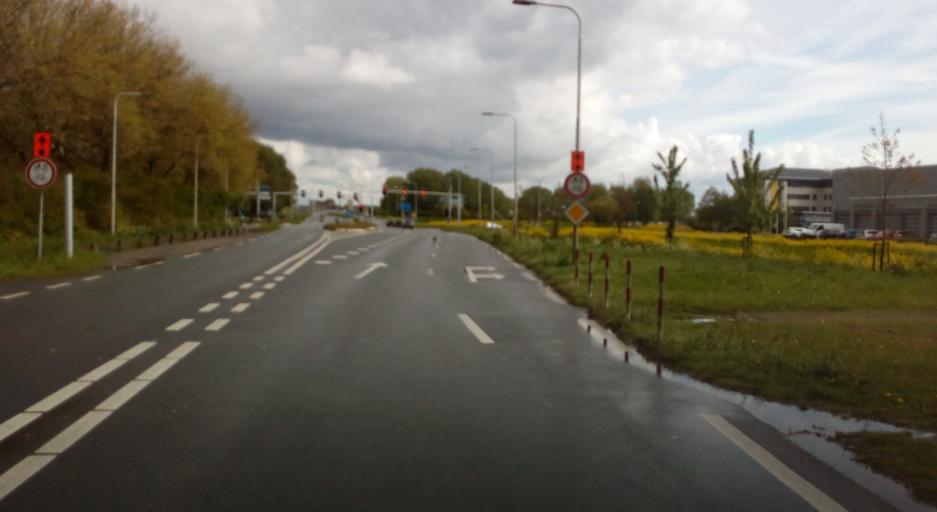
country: NL
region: South Holland
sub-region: Gemeente Zwijndrecht
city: Zwijndrecht
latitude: 51.8324
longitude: 4.6129
